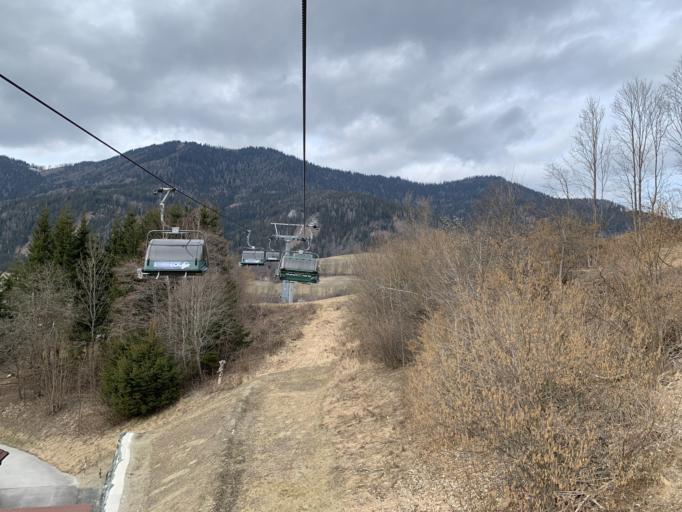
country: AT
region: Styria
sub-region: Politischer Bezirk Bruck-Muerzzuschlag
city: Spital am Semmering
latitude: 47.6109
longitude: 15.7588
